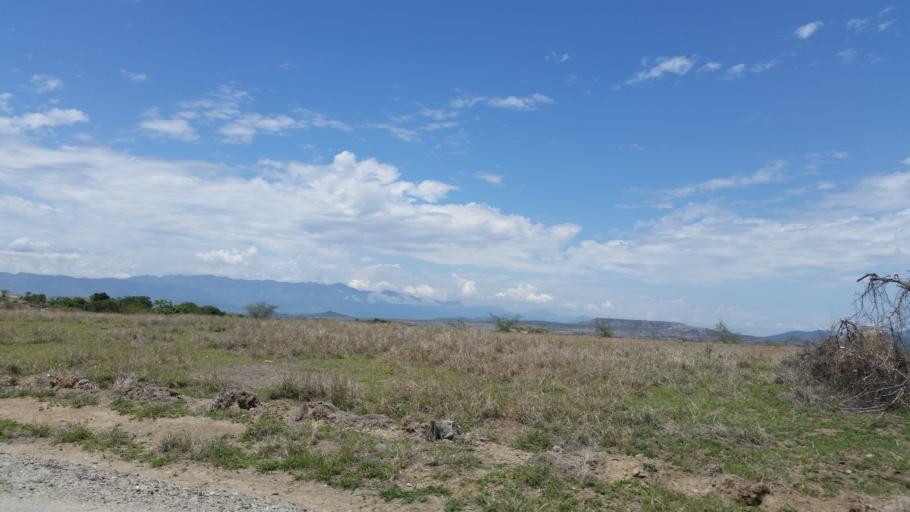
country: CO
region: Huila
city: Baraya
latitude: 3.2366
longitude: -75.1045
